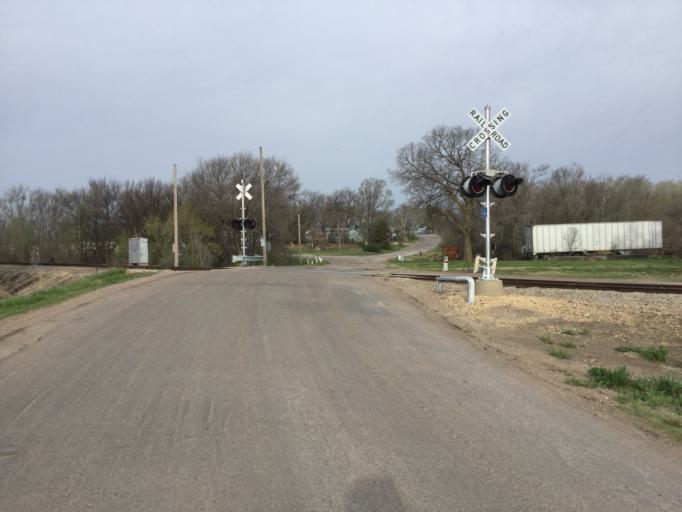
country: US
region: Kansas
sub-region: Norton County
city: Norton
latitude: 39.8300
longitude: -99.8798
